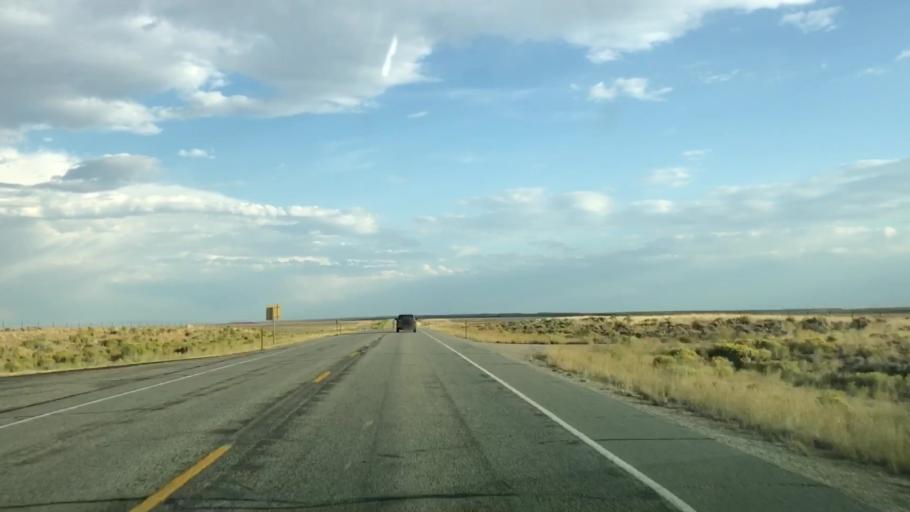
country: US
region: Wyoming
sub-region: Sublette County
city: Marbleton
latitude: 42.3268
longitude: -109.5131
